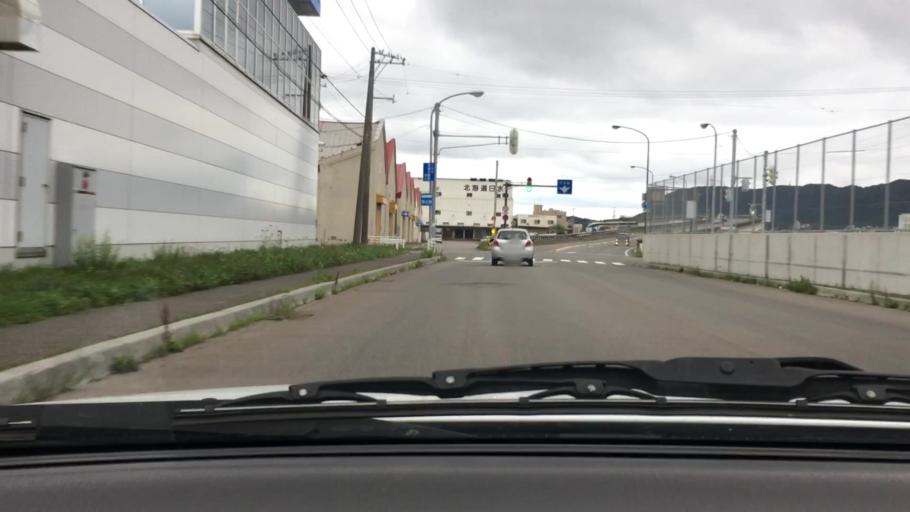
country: JP
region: Hokkaido
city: Hakodate
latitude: 41.7869
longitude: 140.7282
